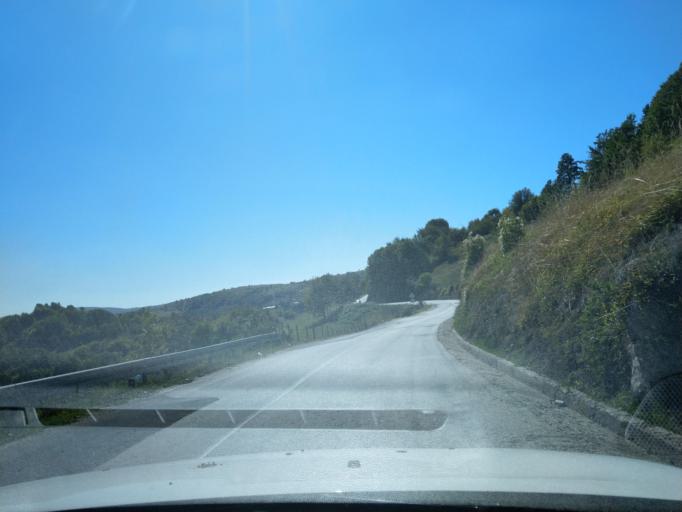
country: RS
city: Sokolovica
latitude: 43.2606
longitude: 20.2331
